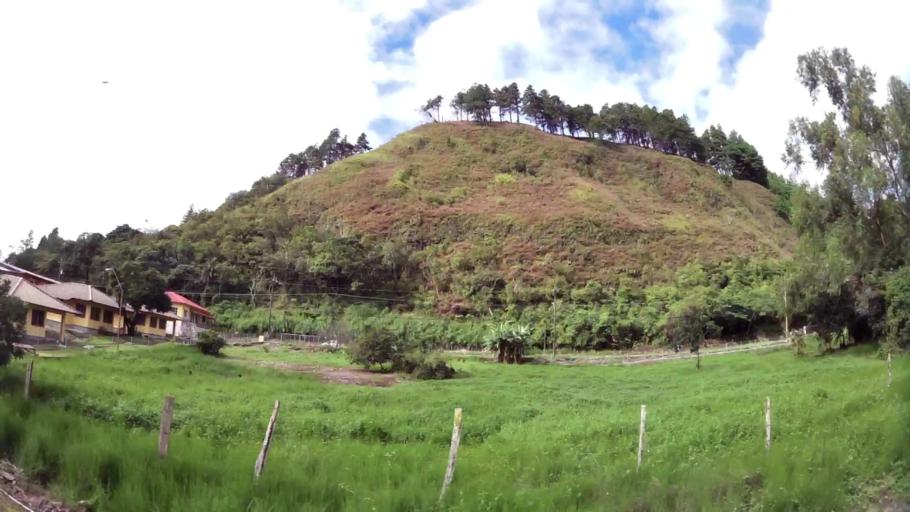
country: PA
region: Chiriqui
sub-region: Distrito Boquete
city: Boquete
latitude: 8.7840
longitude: -82.4340
